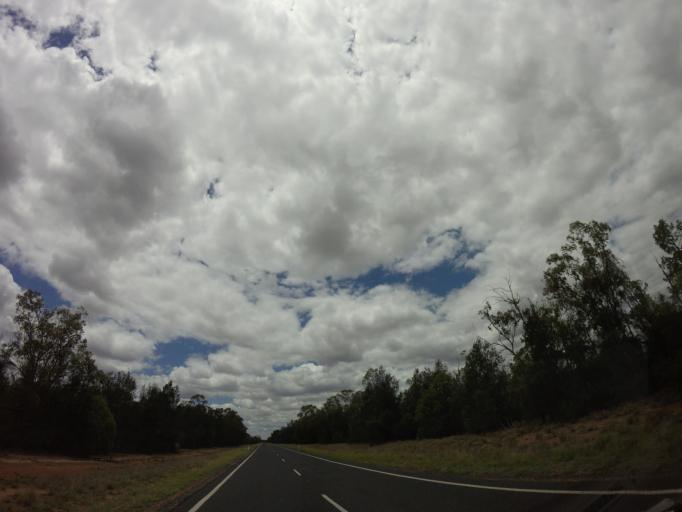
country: AU
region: Queensland
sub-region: Goondiwindi
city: Goondiwindi
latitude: -28.1642
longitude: 150.6123
